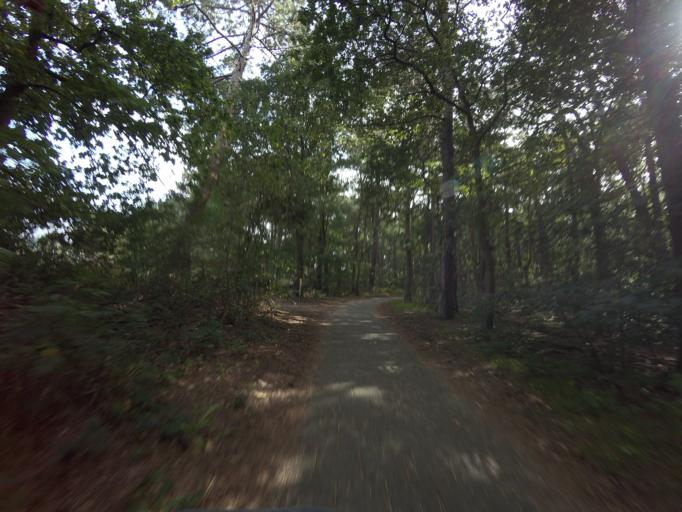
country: NL
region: North Holland
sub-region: Gemeente Texel
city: Den Burg
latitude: 53.0793
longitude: 4.7593
